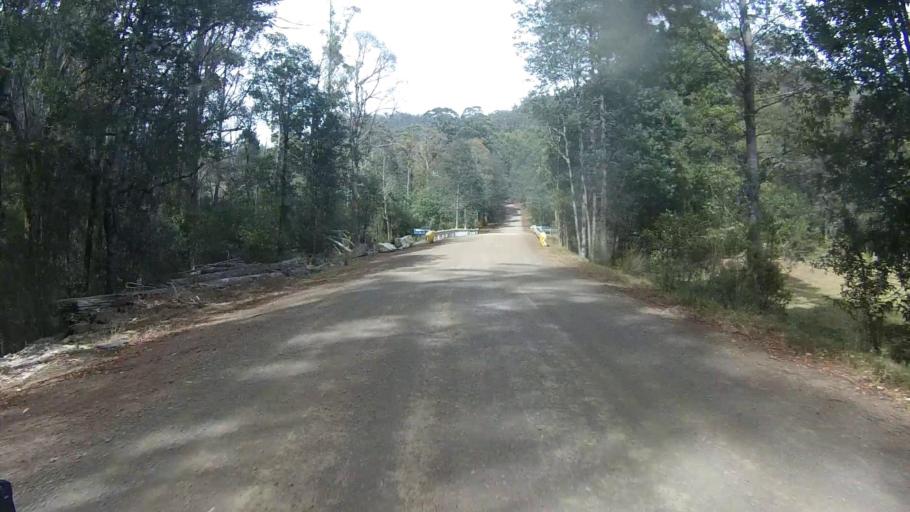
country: AU
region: Tasmania
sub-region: Sorell
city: Sorell
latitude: -42.6923
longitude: 147.8629
